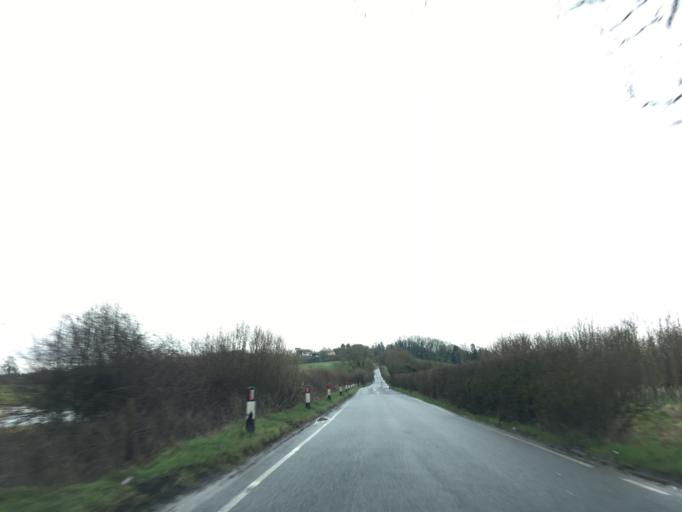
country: GB
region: England
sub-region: Borough of Swindon
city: Wanborough
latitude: 51.5437
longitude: -1.7149
